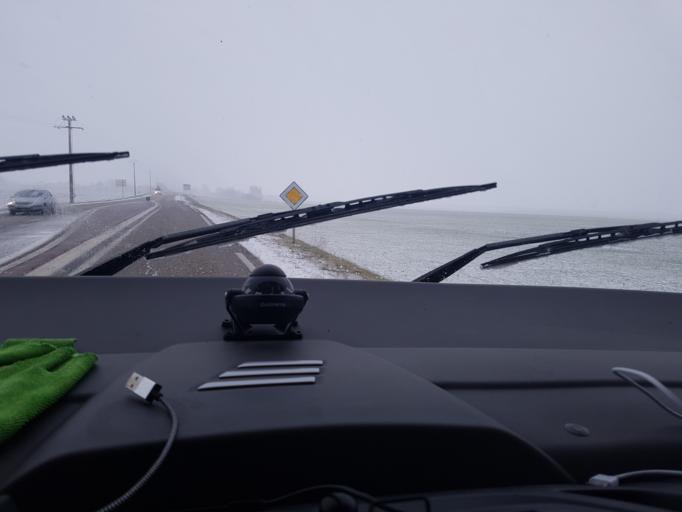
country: FR
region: Lorraine
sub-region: Departement de la Moselle
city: Chateau-Salins
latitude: 48.8686
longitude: 6.4255
